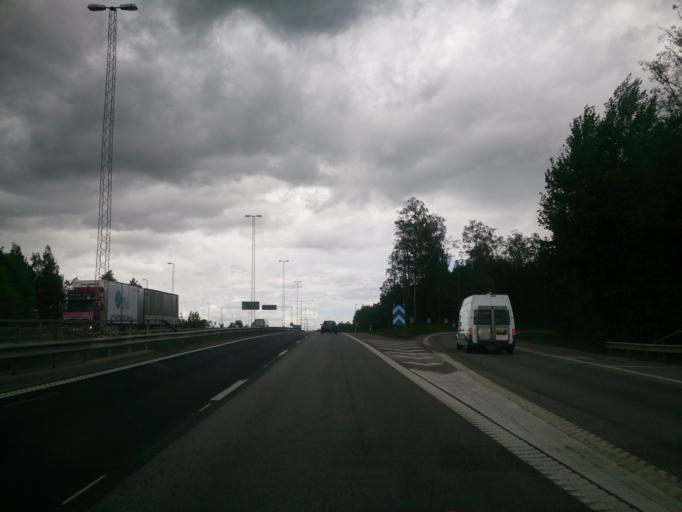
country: SE
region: OEstergoetland
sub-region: Norrkopings Kommun
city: Norrkoping
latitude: 58.5830
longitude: 16.1403
